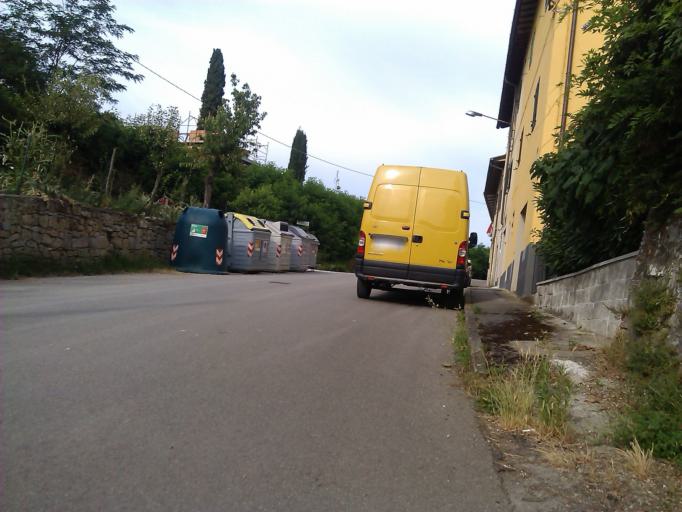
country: IT
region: Tuscany
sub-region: Province of Arezzo
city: Bucine
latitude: 43.4972
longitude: 11.6282
